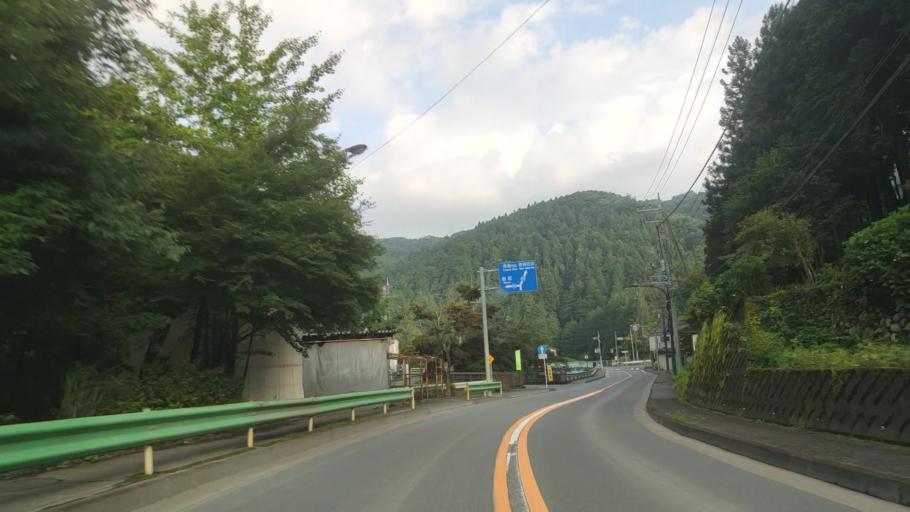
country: JP
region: Tokyo
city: Ome
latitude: 35.8243
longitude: 139.2480
